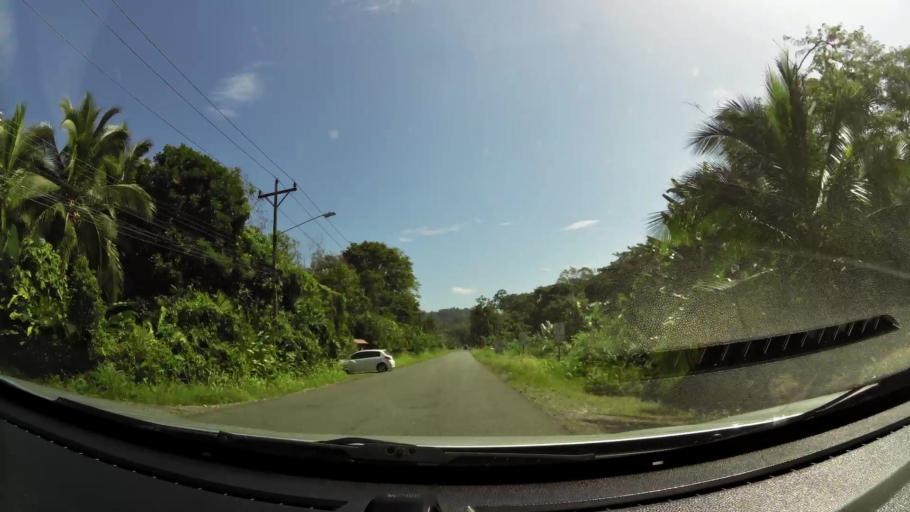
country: PA
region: Bocas del Toro
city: Barranco
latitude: 9.6523
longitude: -82.7946
